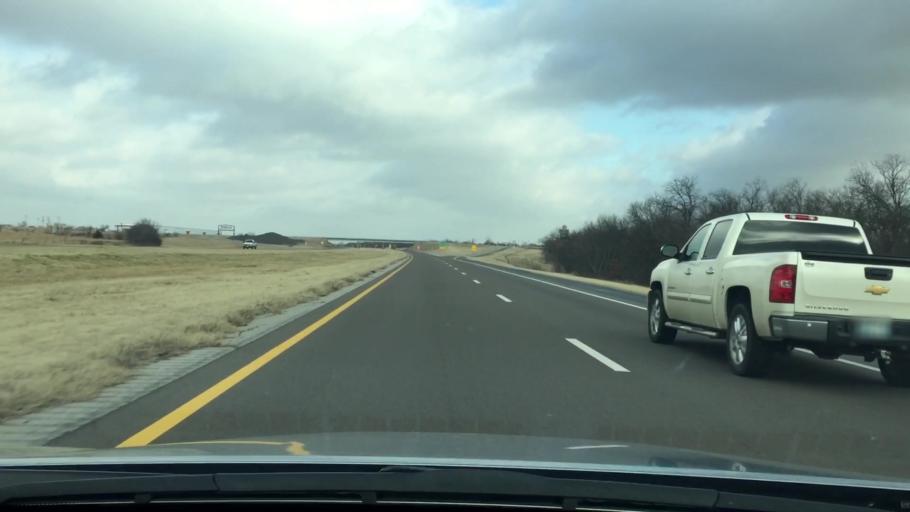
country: US
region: Oklahoma
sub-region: Garvin County
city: Maysville
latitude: 34.8203
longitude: -97.3075
